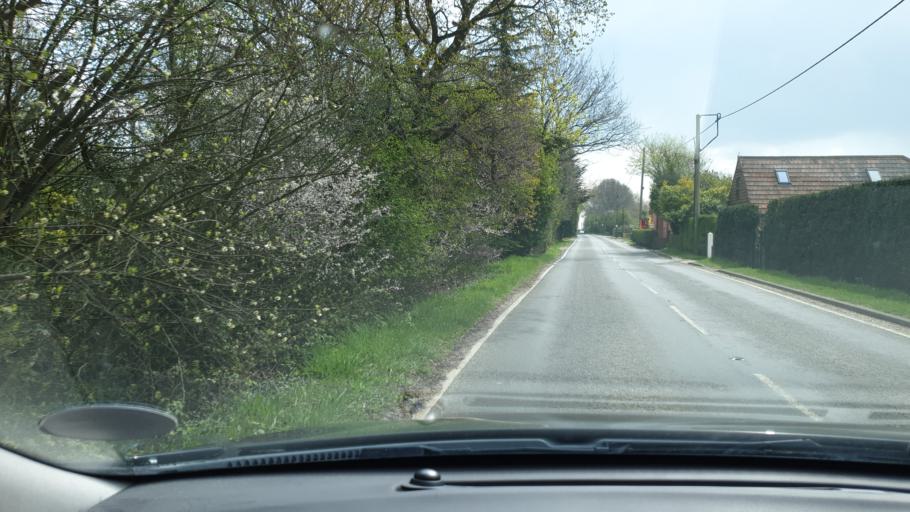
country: GB
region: England
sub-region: Essex
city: Alresford
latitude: 51.9117
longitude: 0.9998
